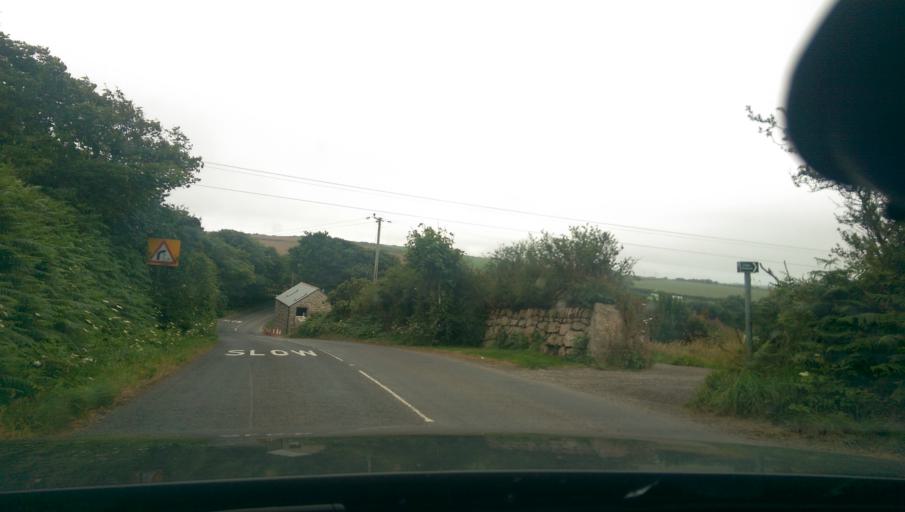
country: GB
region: England
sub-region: Cornwall
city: St. Buryan
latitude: 50.0919
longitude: -5.6250
